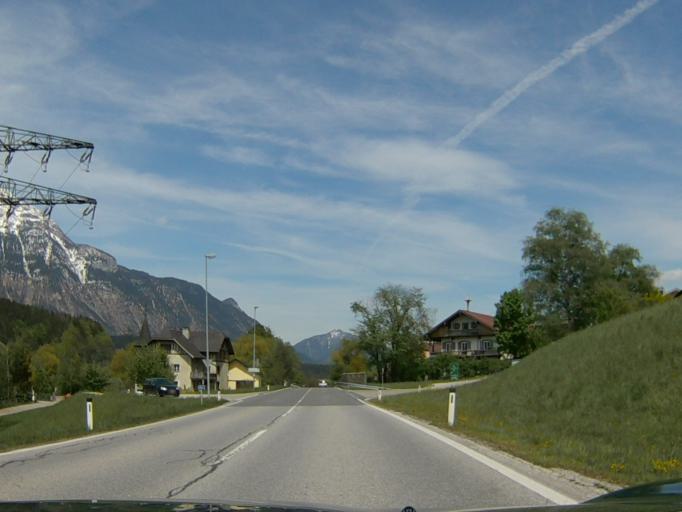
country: AT
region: Tyrol
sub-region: Politischer Bezirk Schwaz
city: Wiesing
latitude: 47.3893
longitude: 11.7942
